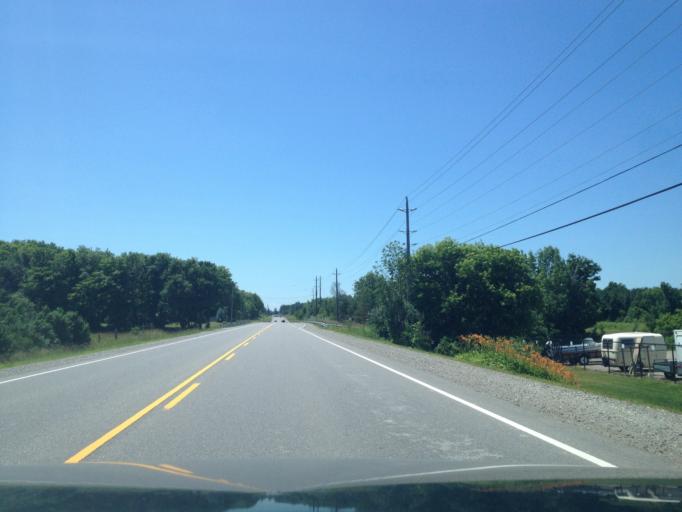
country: CA
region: Ontario
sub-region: Wellington County
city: Guelph
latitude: 43.6173
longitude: -80.0985
